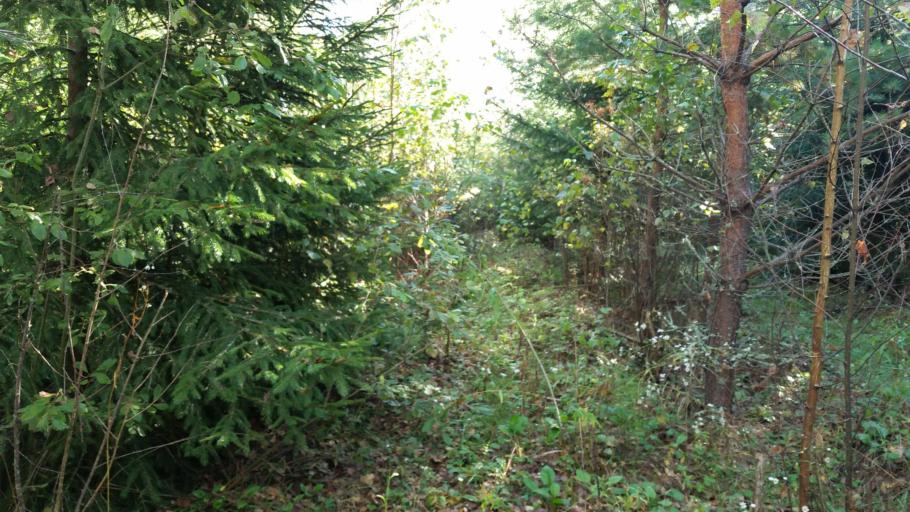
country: BY
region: Vitebsk
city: Vitebsk
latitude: 54.9771
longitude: 30.3408
